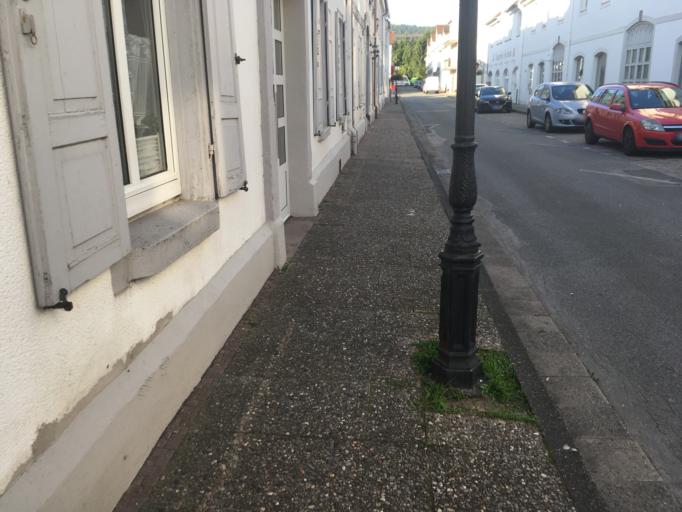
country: DE
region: Lower Saxony
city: Bad Karlshafen
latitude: 51.6422
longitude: 9.4534
